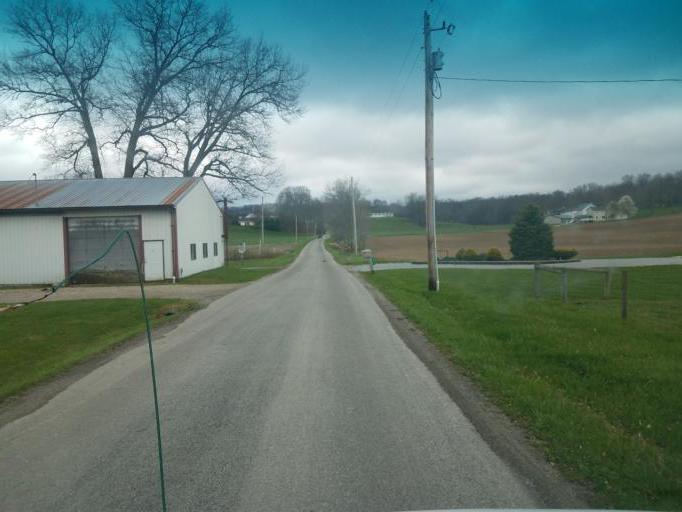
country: US
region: Ohio
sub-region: Stark County
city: Beach City
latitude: 40.6350
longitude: -81.6781
